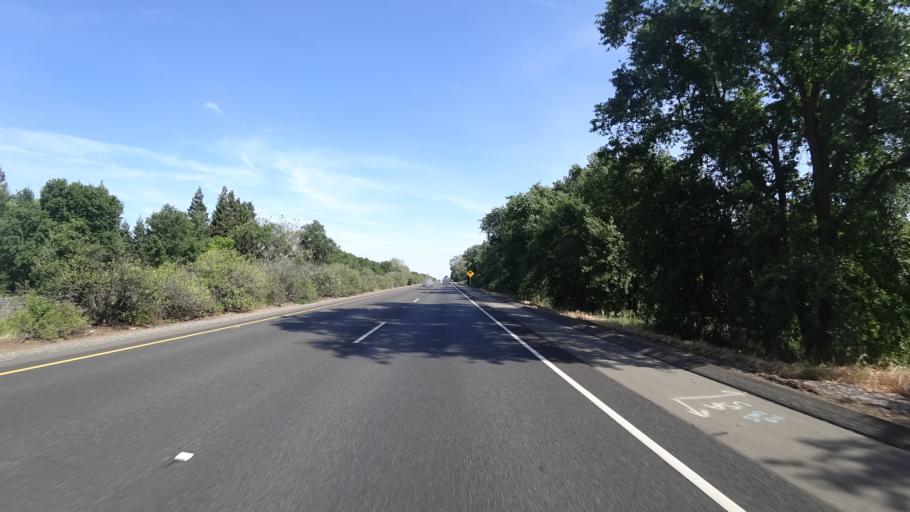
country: US
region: California
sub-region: Butte County
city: Chico
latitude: 39.7661
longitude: -121.8632
